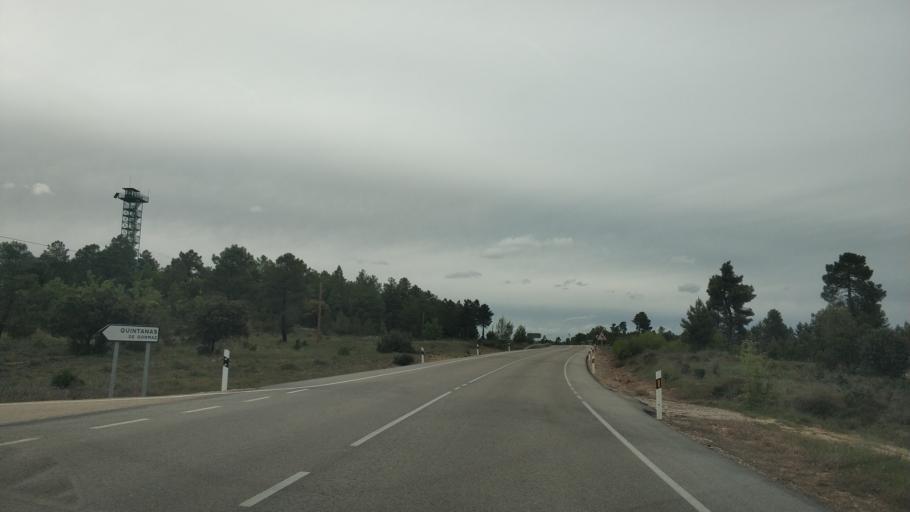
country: ES
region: Castille and Leon
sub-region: Provincia de Soria
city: Quintanas de Gormaz
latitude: 41.5331
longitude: -2.9495
